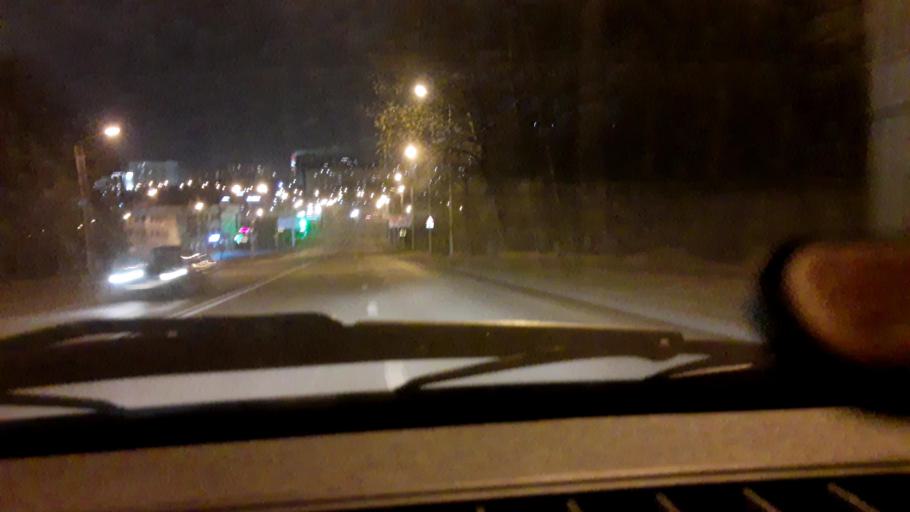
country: RU
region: Bashkortostan
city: Ufa
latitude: 54.7281
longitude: 56.0034
